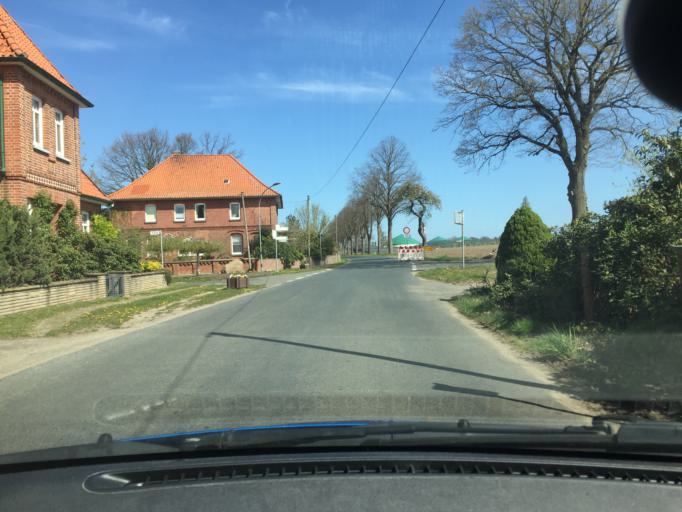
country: DE
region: Lower Saxony
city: Suhlendorf
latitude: 52.9243
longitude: 10.7110
